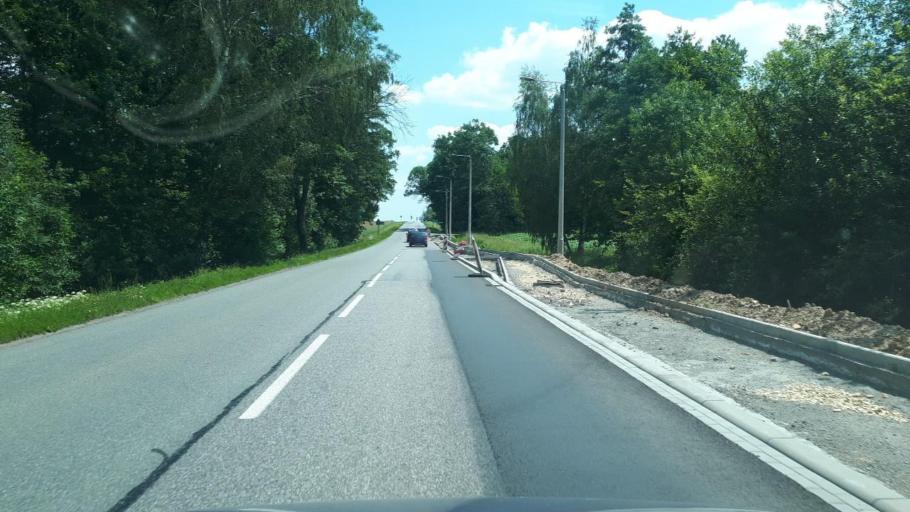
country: PL
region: Silesian Voivodeship
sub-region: Powiat pszczynski
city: Miedzna
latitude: 49.9703
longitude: 19.0250
